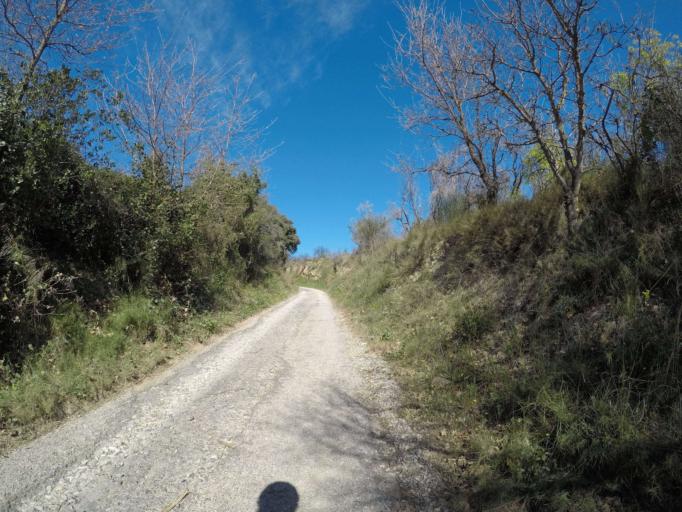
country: FR
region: Languedoc-Roussillon
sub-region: Departement des Pyrenees-Orientales
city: Millas
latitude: 42.7023
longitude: 2.6824
